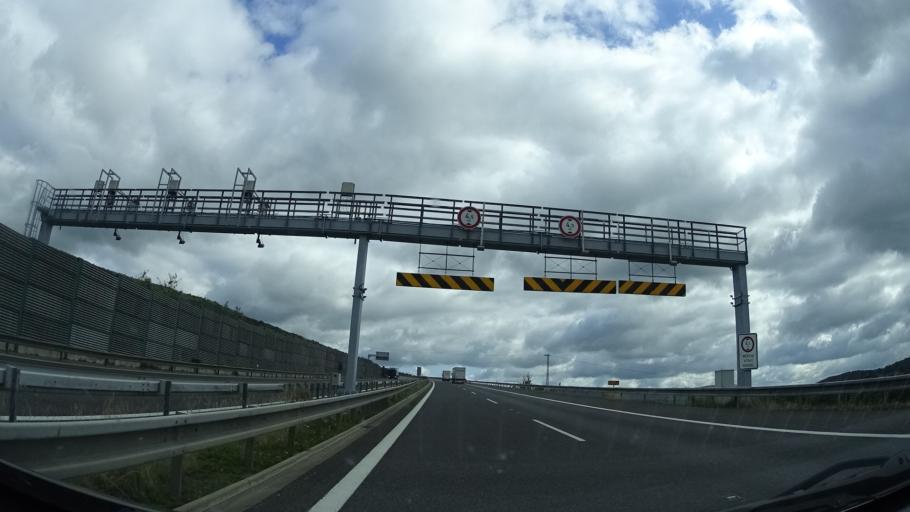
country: CZ
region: Ustecky
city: Libouchec
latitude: 50.7313
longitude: 14.0065
